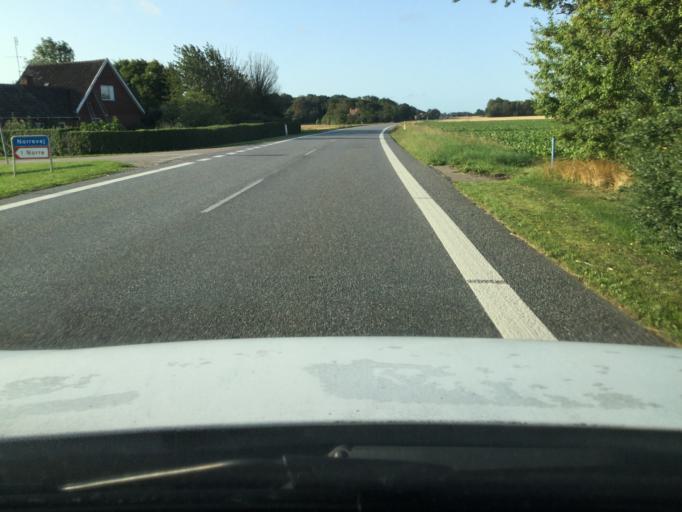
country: DK
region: Zealand
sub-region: Lolland Kommune
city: Rodby
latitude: 54.7356
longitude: 11.3895
